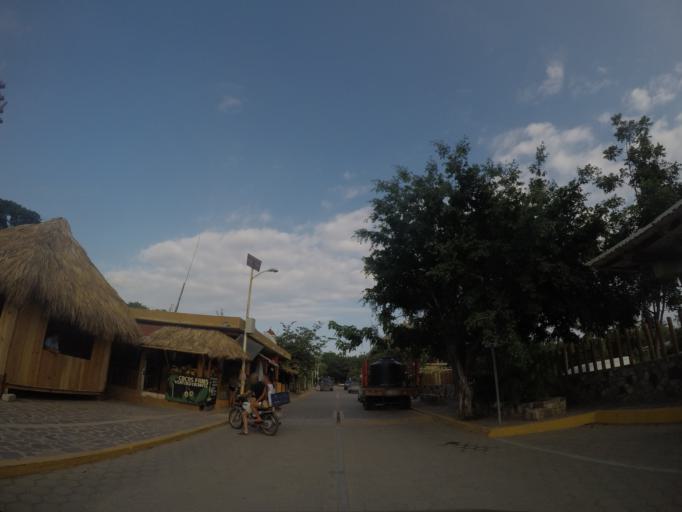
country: MX
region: Oaxaca
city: Santa Maria Tonameca
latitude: 15.6672
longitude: -96.5537
